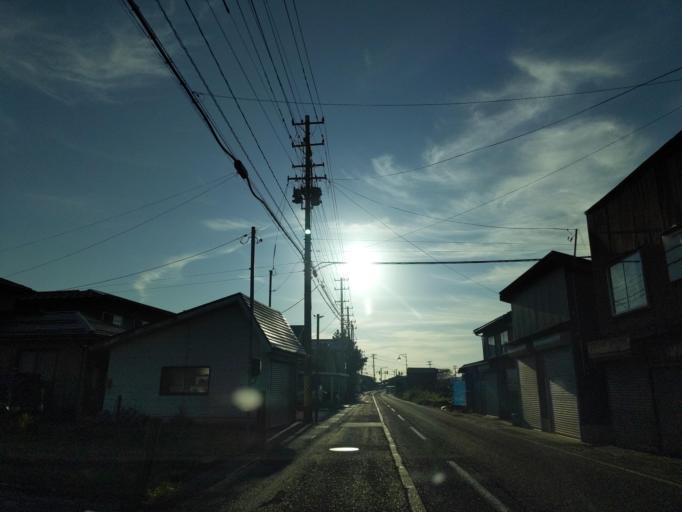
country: JP
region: Niigata
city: Nagaoka
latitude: 37.5794
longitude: 138.7697
